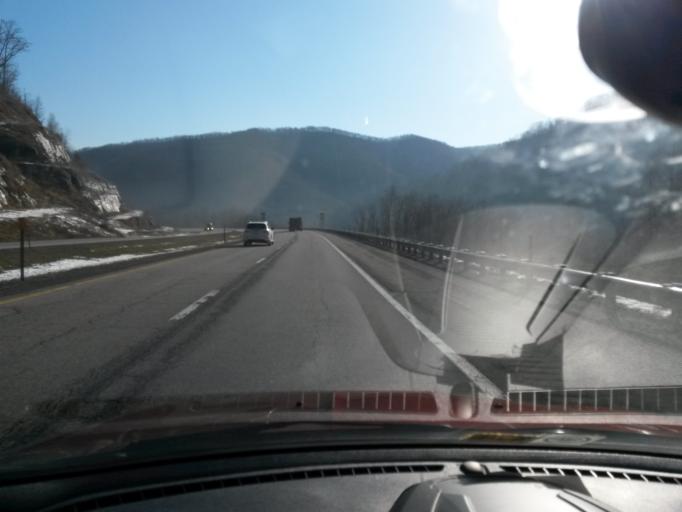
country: US
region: West Virginia
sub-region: Nicholas County
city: Craigsville
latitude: 38.4801
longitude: -80.7665
